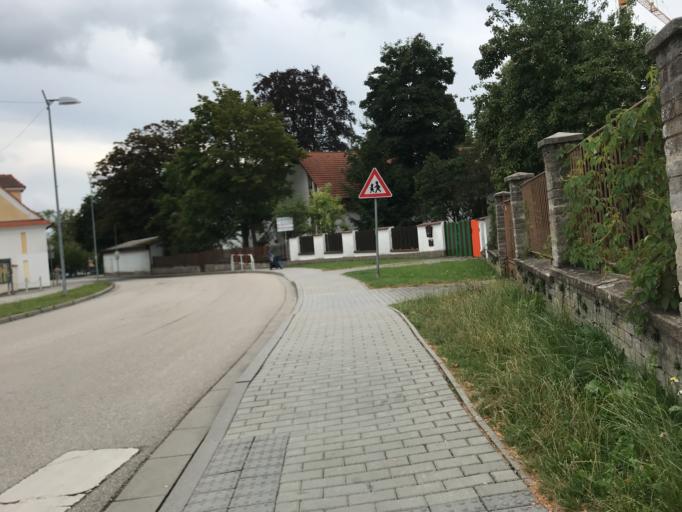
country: CZ
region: Jihocesky
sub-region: Okres Jindrichuv Hradec
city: Trebon
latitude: 49.0073
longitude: 14.7655
